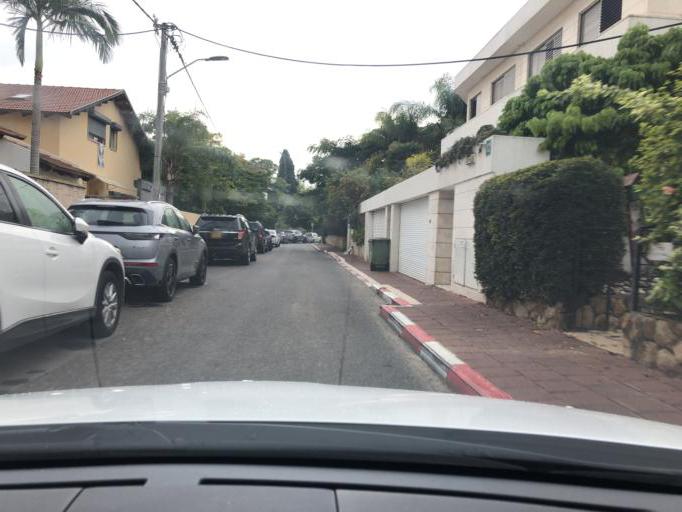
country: IL
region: Tel Aviv
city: Giv`atayim
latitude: 32.0579
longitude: 34.8202
